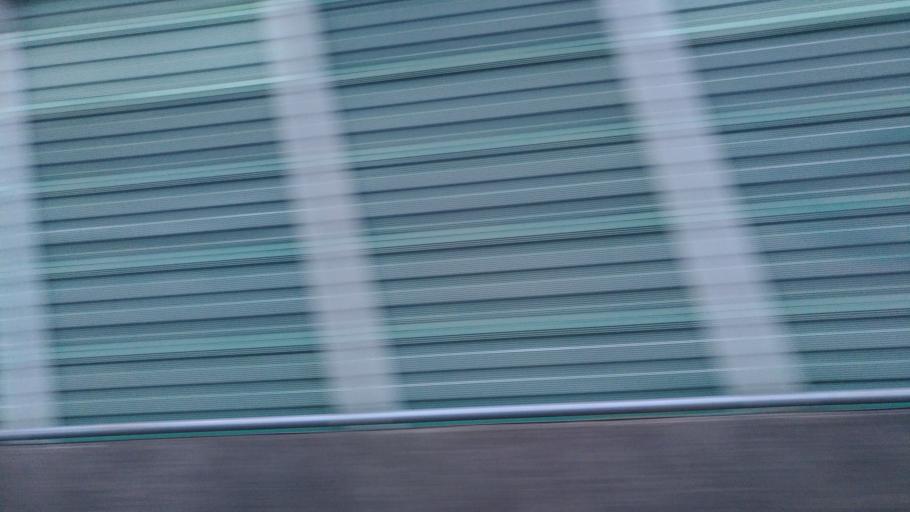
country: TW
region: Taiwan
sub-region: Hsinchu
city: Hsinchu
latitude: 24.7543
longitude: 120.9520
